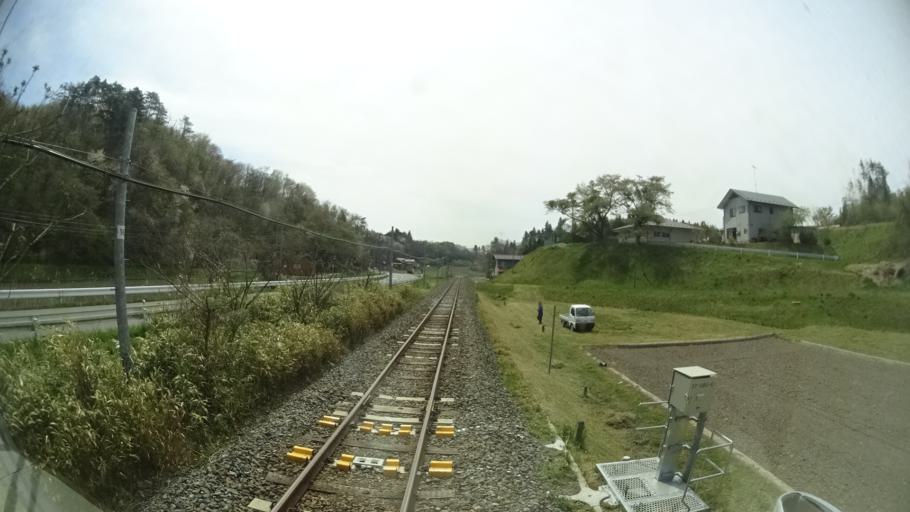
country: JP
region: Iwate
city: Ichinoseki
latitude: 38.9463
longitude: 141.3373
